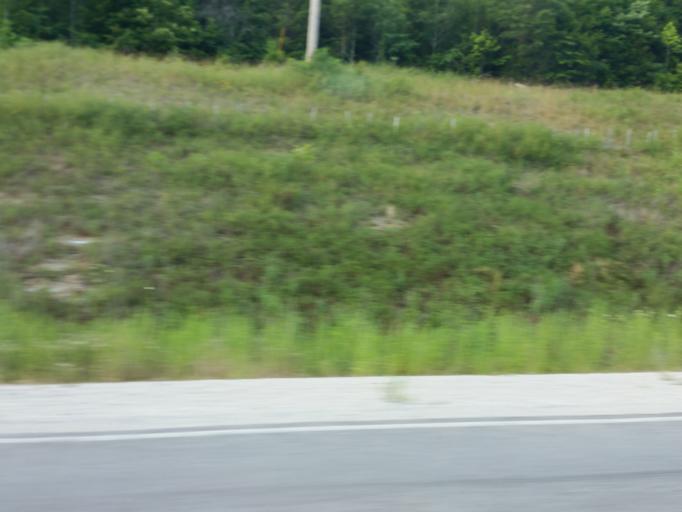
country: US
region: Tennessee
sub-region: Maury County
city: Mount Pleasant
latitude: 35.5646
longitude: -87.3678
